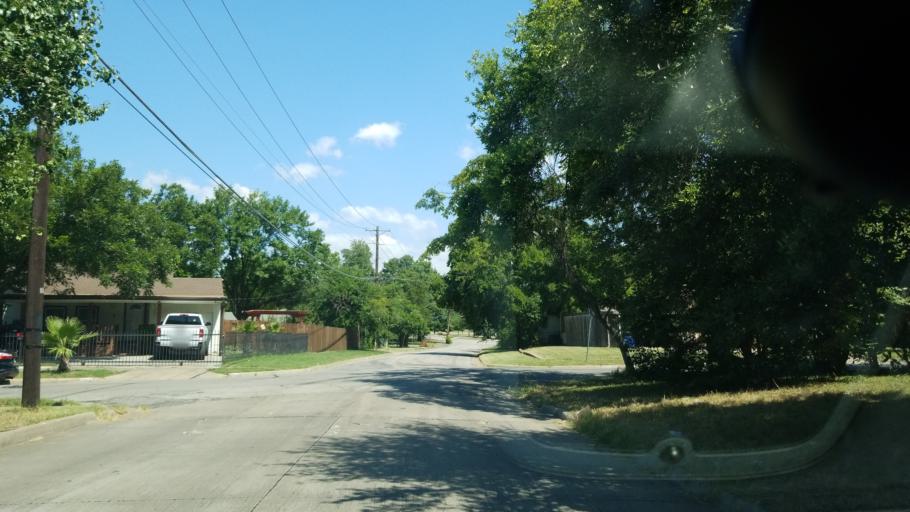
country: US
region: Texas
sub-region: Dallas County
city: Cockrell Hill
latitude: 32.7180
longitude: -96.8361
